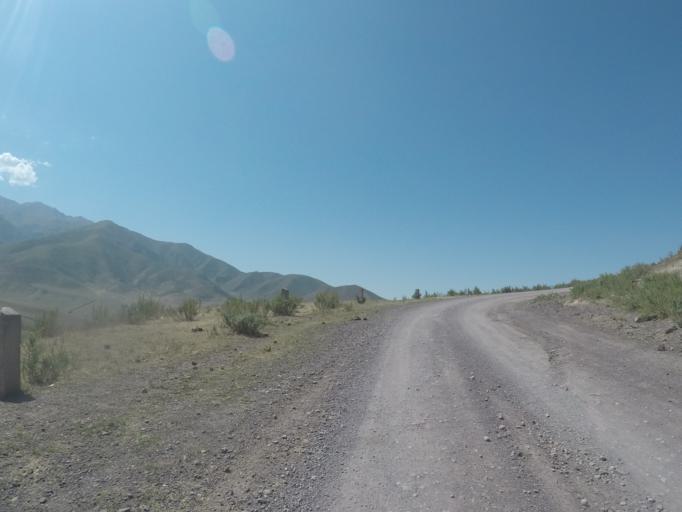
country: KG
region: Chuy
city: Bishkek
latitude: 42.6509
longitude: 74.5159
